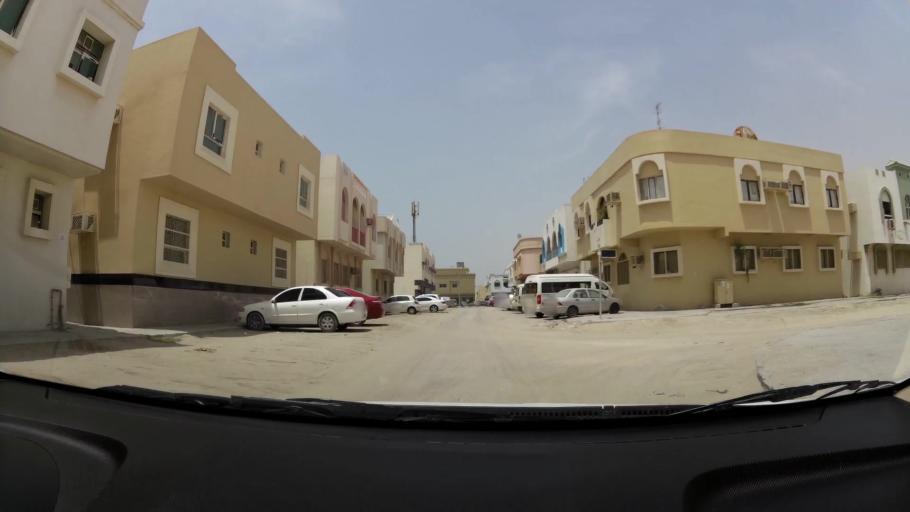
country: AE
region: Ash Shariqah
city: Sharjah
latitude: 25.3523
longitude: 55.4044
